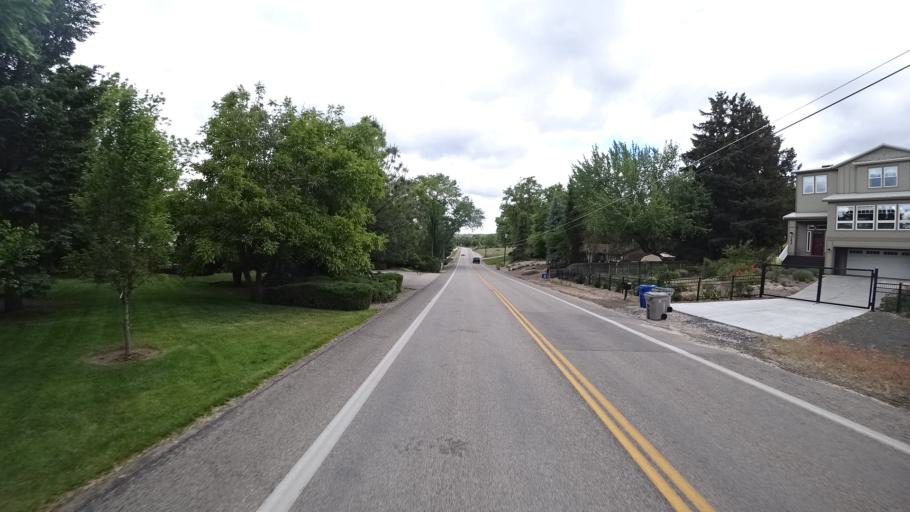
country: US
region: Idaho
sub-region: Ada County
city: Garden City
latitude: 43.6751
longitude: -116.2620
